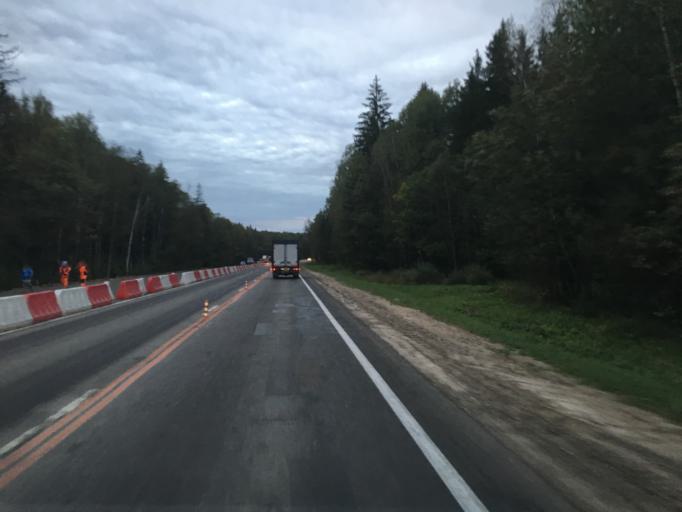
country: RU
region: Kaluga
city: Detchino
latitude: 54.7043
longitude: 36.2914
